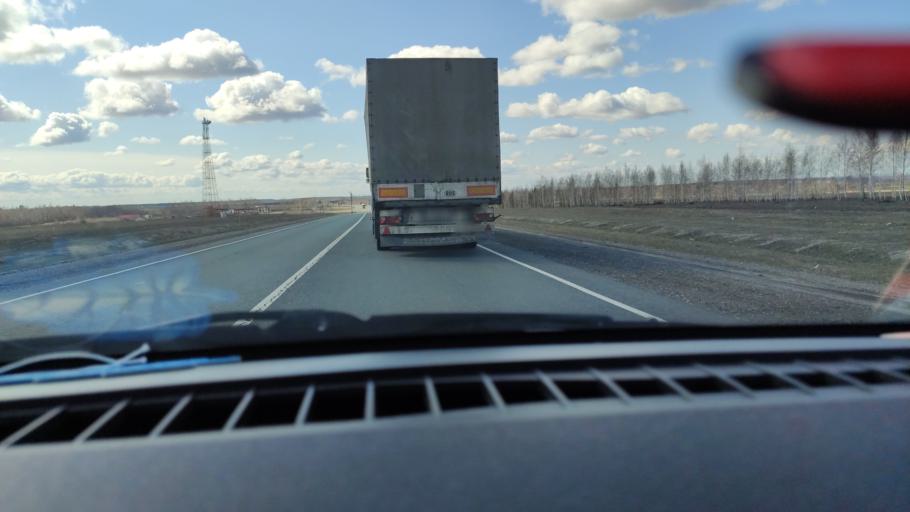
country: RU
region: Samara
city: Syzran'
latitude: 52.9274
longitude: 48.3049
